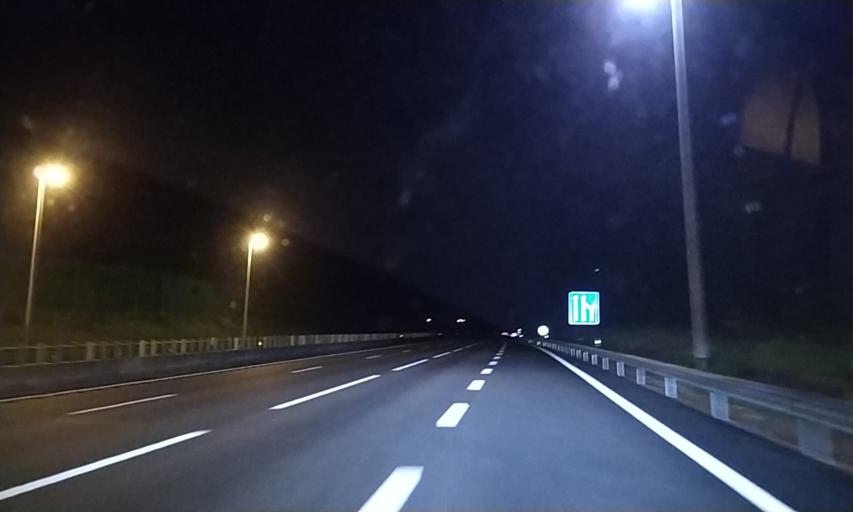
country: PT
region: Aveiro
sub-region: Mealhada
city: Mealhada
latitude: 40.3345
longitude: -8.4934
